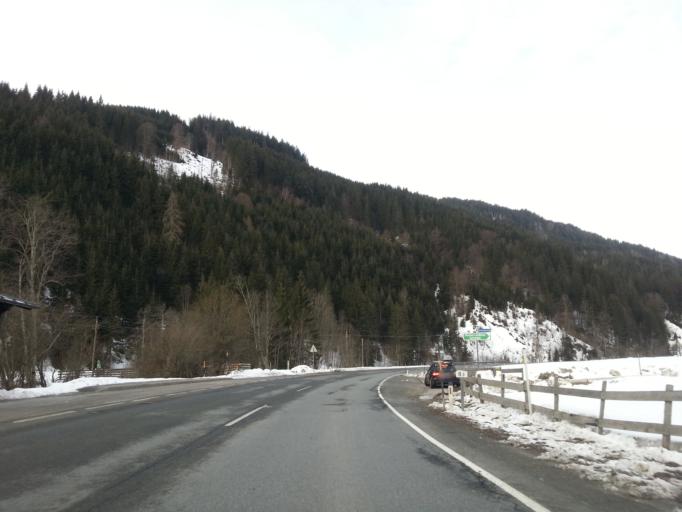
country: AT
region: Salzburg
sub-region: Politischer Bezirk Zell am See
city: Viehhofen
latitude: 47.3688
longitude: 12.7014
